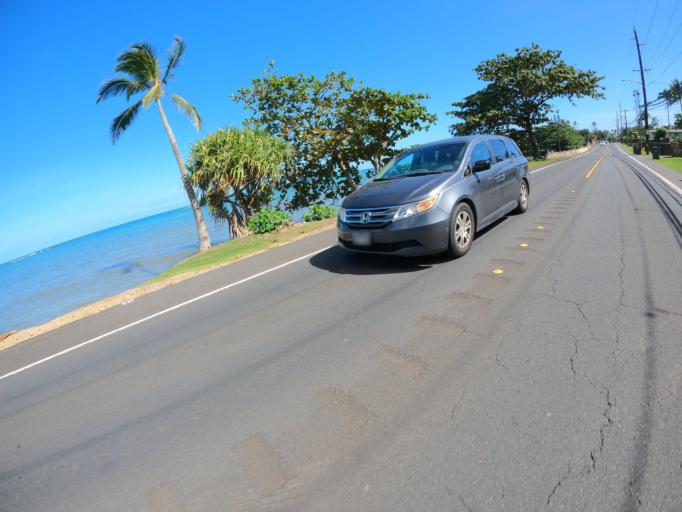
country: US
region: Hawaii
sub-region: Honolulu County
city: Ka'a'awa
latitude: 21.5578
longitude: -157.8571
